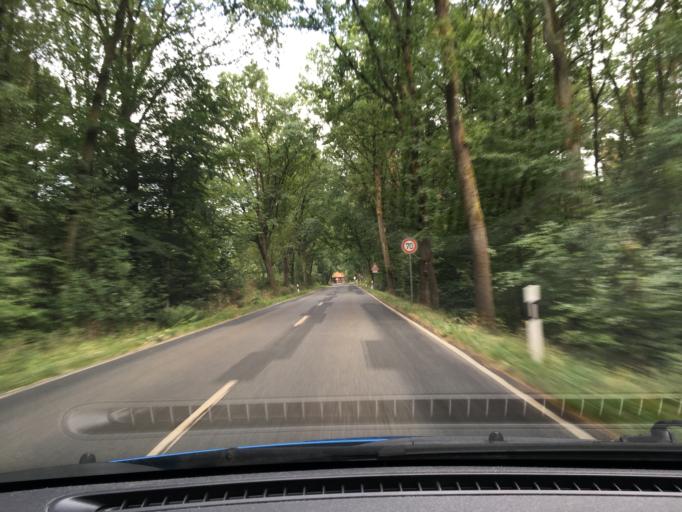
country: DE
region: Lower Saxony
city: Undeloh
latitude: 53.1991
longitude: 9.9691
